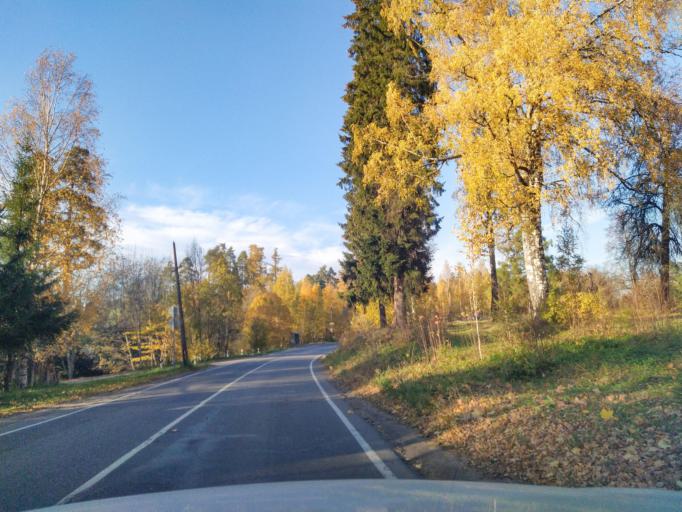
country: RU
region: Leningrad
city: Siverskiy
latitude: 59.3445
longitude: 30.0569
